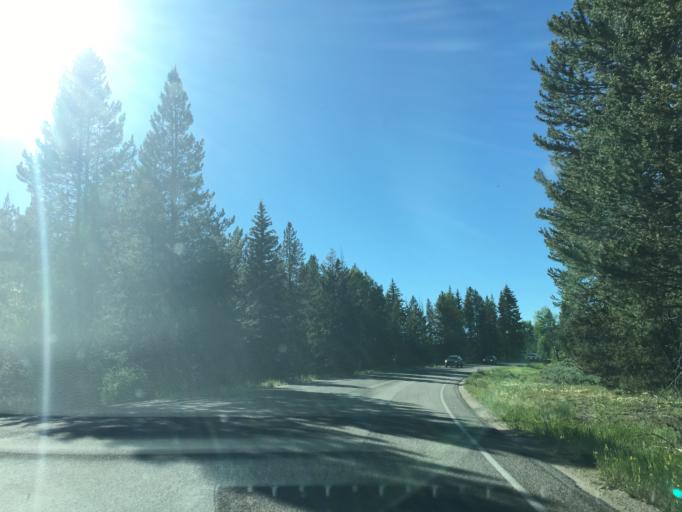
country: US
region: Wyoming
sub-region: Teton County
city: Jackson
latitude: 43.8458
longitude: -110.5161
